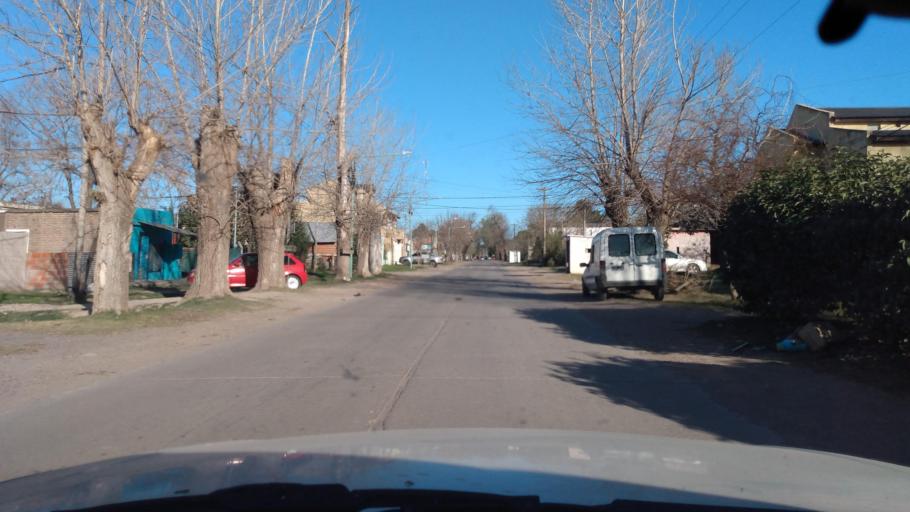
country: AR
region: Buenos Aires
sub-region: Partido de Lujan
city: Lujan
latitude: -34.6234
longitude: -59.2552
